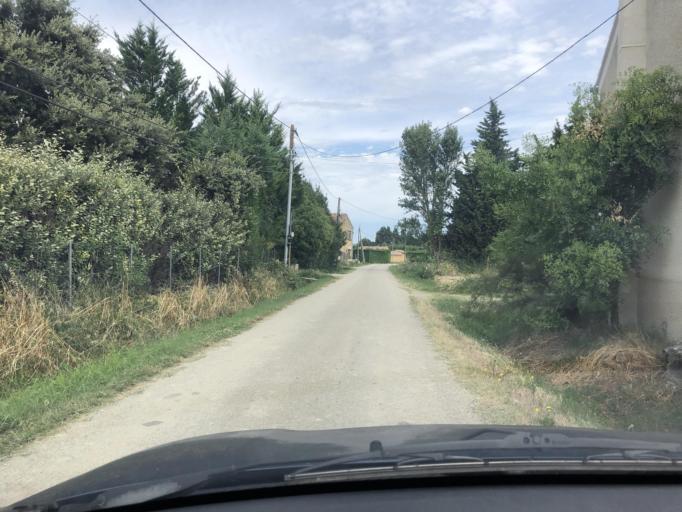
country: FR
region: Provence-Alpes-Cote d'Azur
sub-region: Departement du Vaucluse
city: Piolenc
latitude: 44.1606
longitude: 4.7617
